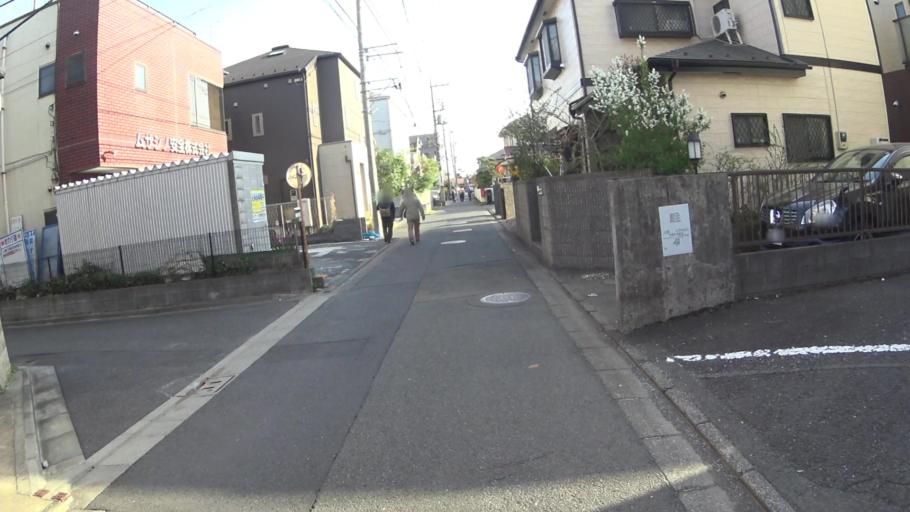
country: JP
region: Tokyo
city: Kokubunji
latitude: 35.7139
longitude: 139.5021
